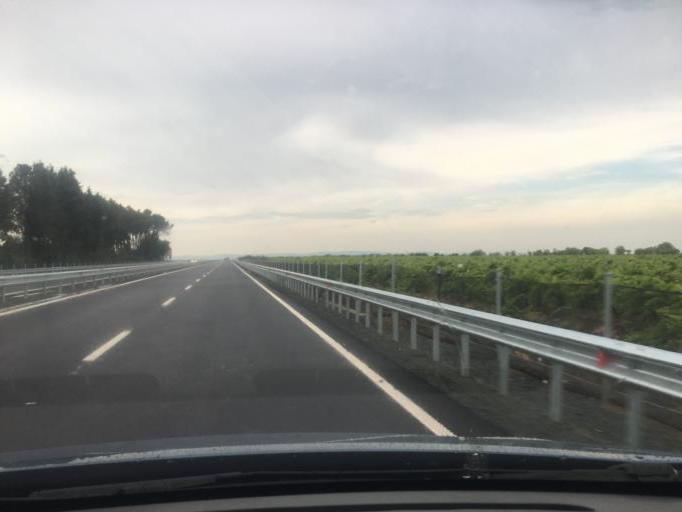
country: BG
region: Burgas
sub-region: Obshtina Pomorie
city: Pomorie
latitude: 42.5972
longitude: 27.6159
